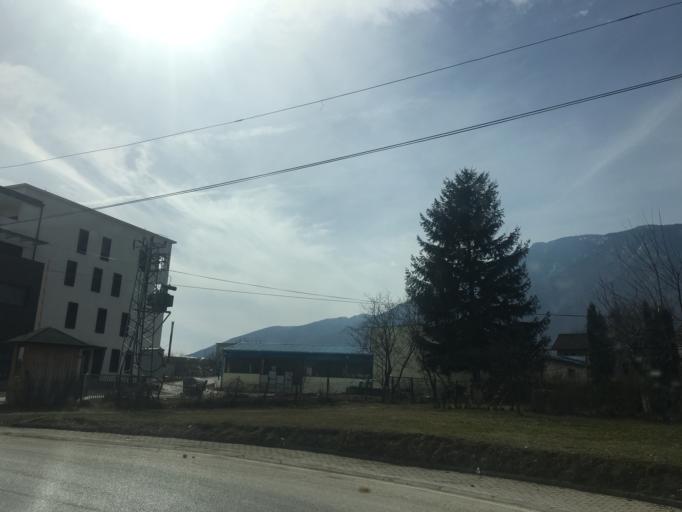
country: XK
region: Pec
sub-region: Komuna e Pejes
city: Peje
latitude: 42.6411
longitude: 20.2940
